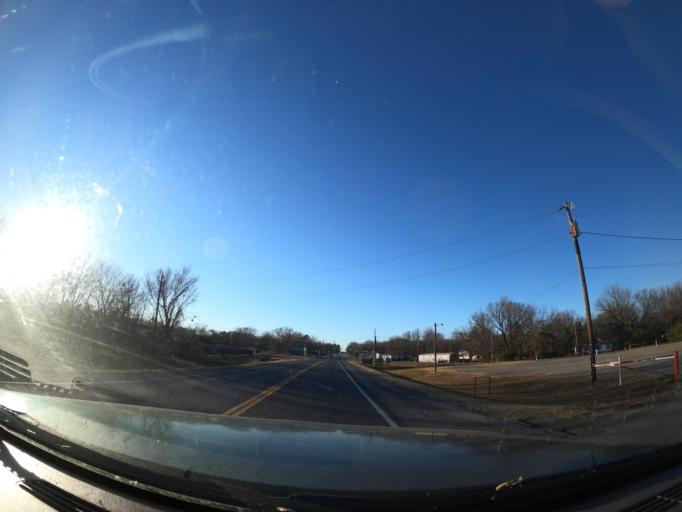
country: US
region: Oklahoma
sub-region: Pittsburg County
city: Hartshorne
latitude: 34.8413
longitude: -95.5435
